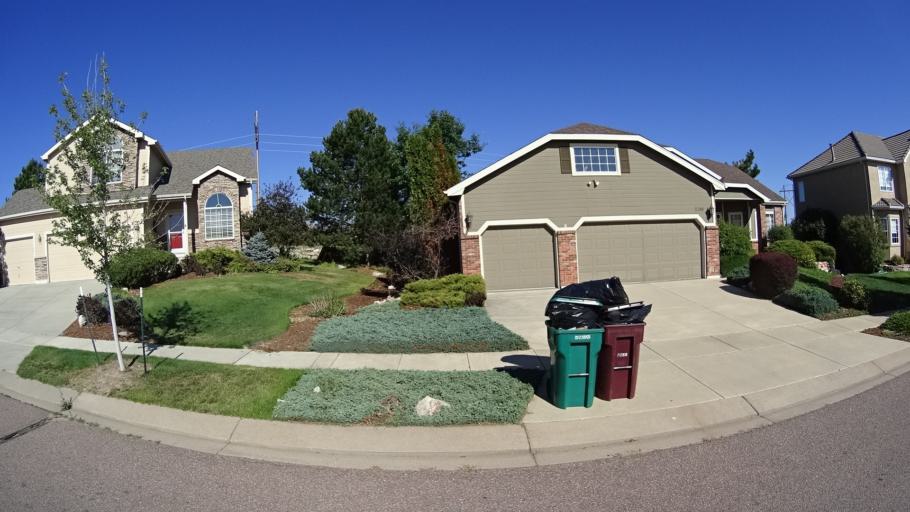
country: US
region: Colorado
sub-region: El Paso County
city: Gleneagle
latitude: 38.9765
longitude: -104.7836
